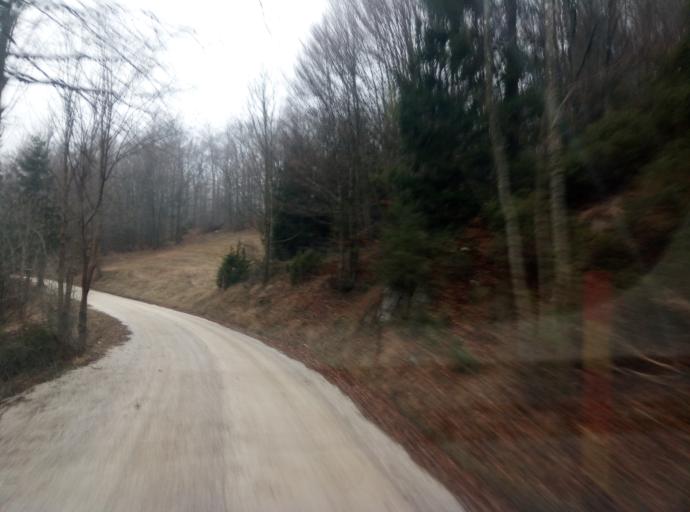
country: SI
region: Vipava
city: Vipava
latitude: 45.8947
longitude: 14.0535
